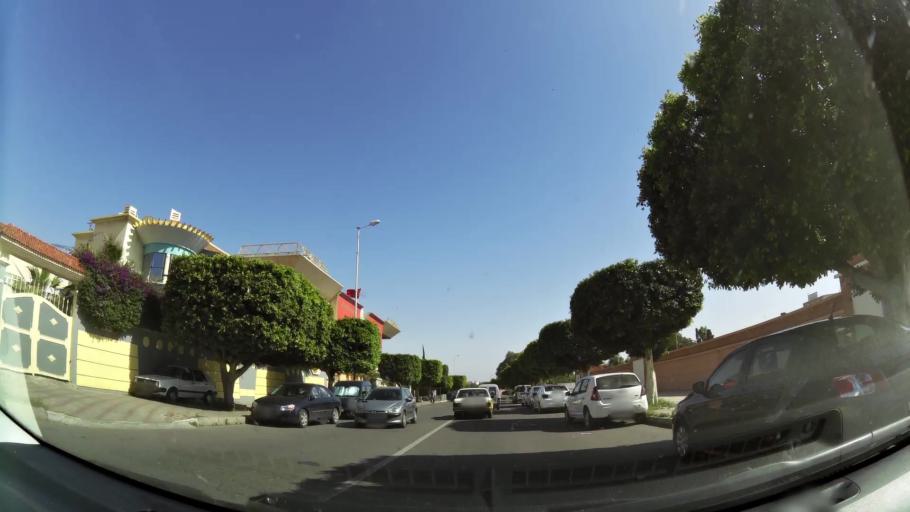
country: MA
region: Souss-Massa-Draa
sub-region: Inezgane-Ait Mellou
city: Inezgane
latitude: 30.3626
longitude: -9.5436
